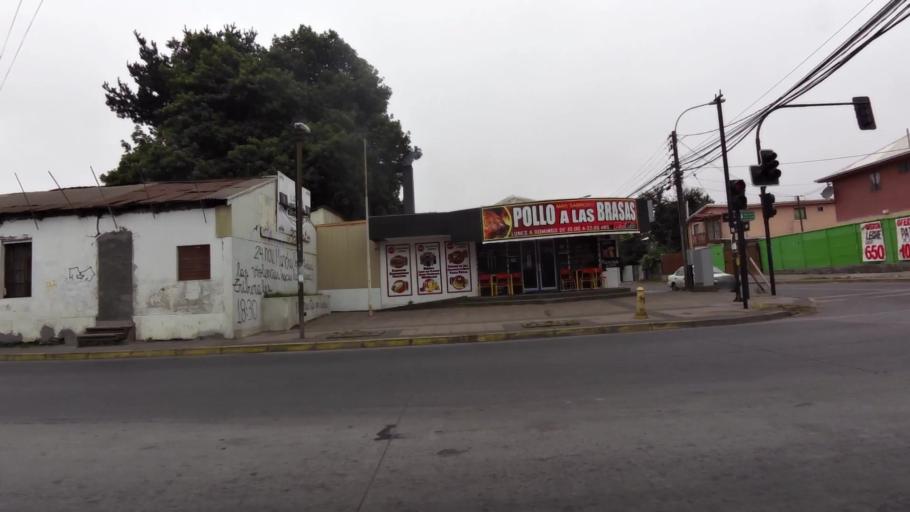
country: CL
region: Biobio
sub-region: Provincia de Concepcion
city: Concepcion
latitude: -36.8086
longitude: -73.0333
